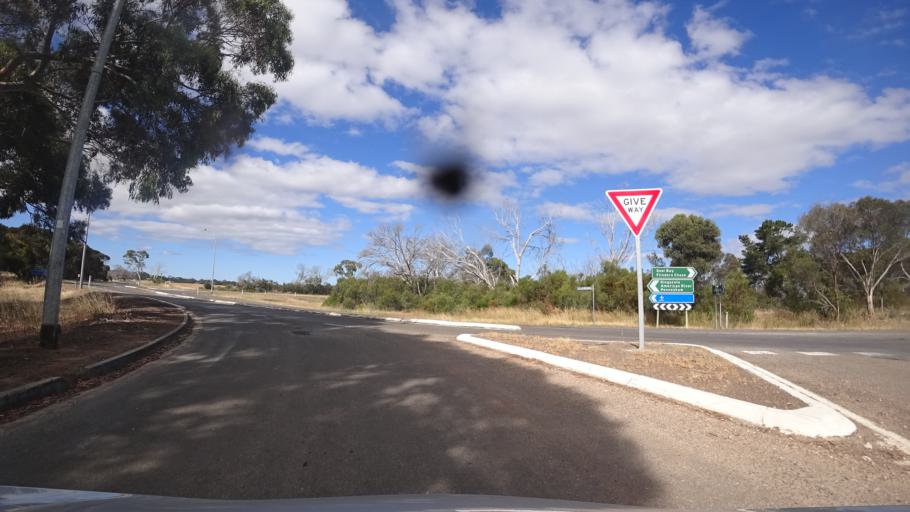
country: AU
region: South Australia
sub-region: Kangaroo Island
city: Kingscote
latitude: -35.7078
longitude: 137.5131
